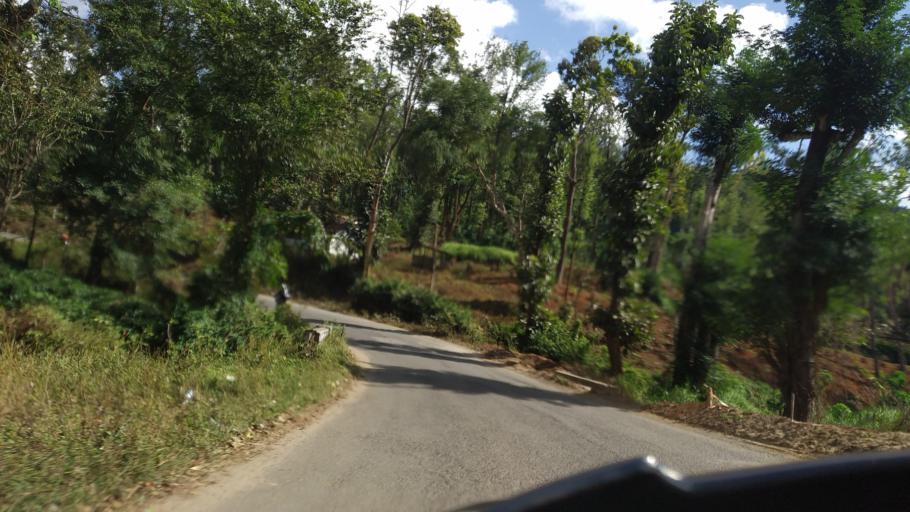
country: IN
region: Karnataka
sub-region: Kodagu
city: Ponnampet
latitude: 11.9633
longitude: 76.0559
